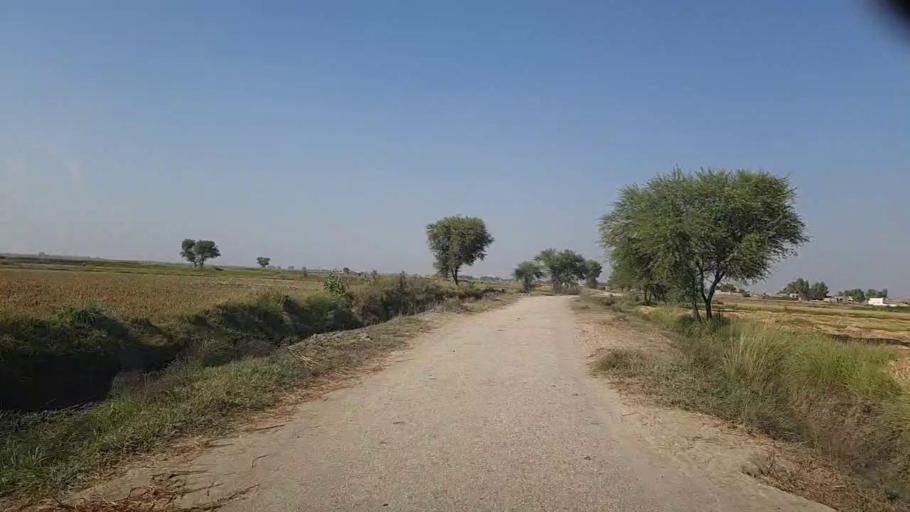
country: PK
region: Sindh
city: Tangwani
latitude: 28.2511
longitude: 68.9398
